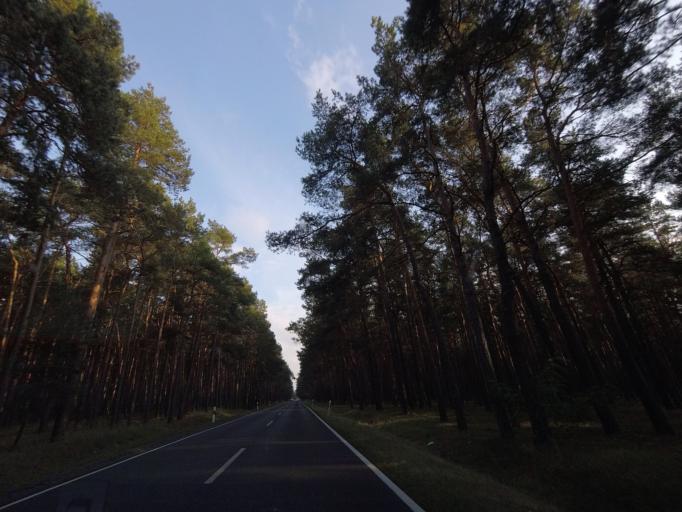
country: DE
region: Brandenburg
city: Linthe
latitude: 52.1666
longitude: 12.7709
